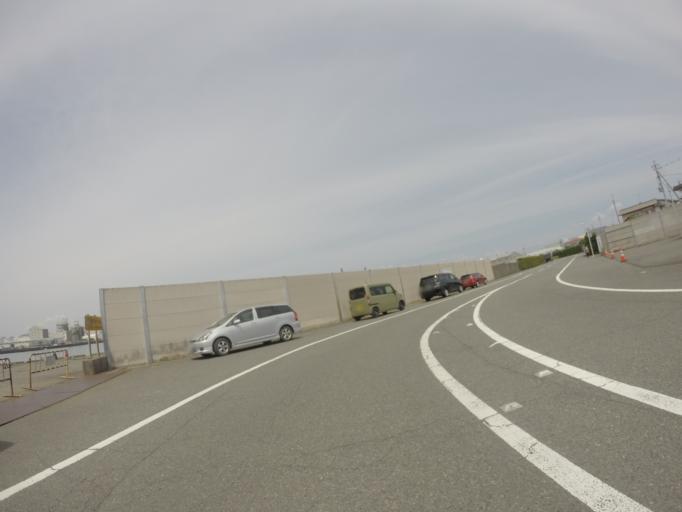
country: JP
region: Shizuoka
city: Fujieda
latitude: 34.7795
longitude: 138.2959
